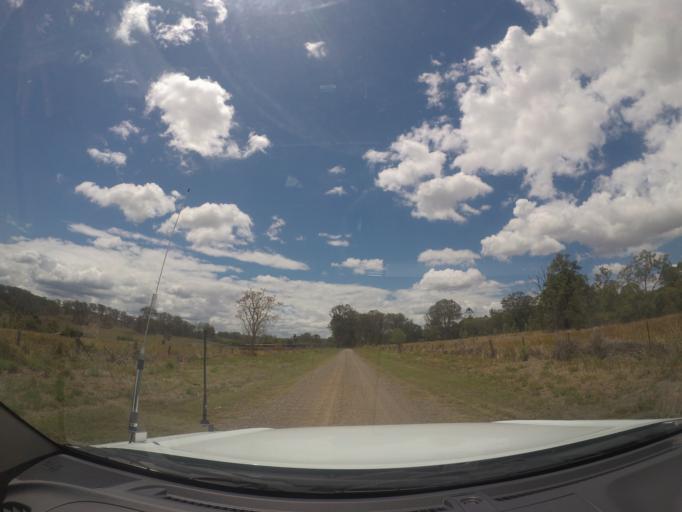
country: AU
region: Queensland
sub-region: Logan
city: Cedar Vale
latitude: -27.9008
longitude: 153.0620
